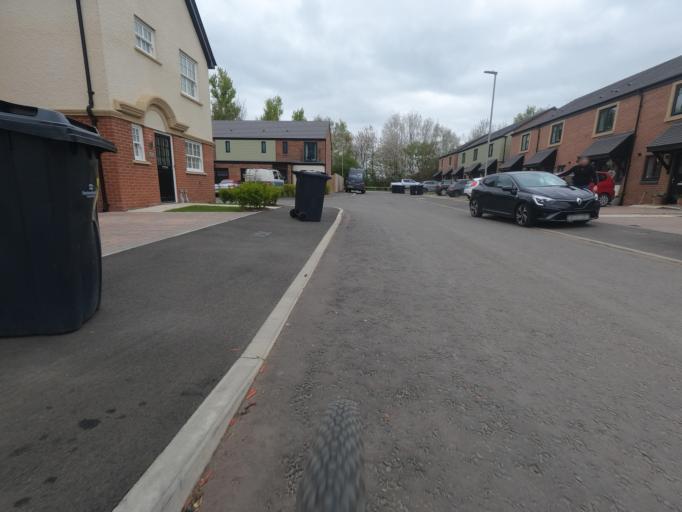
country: GB
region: England
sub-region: Northumberland
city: Ponteland
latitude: 55.0593
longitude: -1.7570
